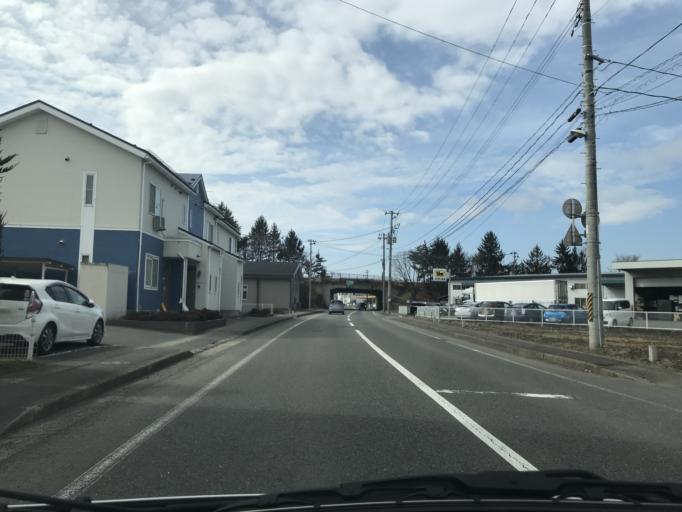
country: JP
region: Iwate
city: Hanamaki
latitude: 39.3796
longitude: 141.0940
